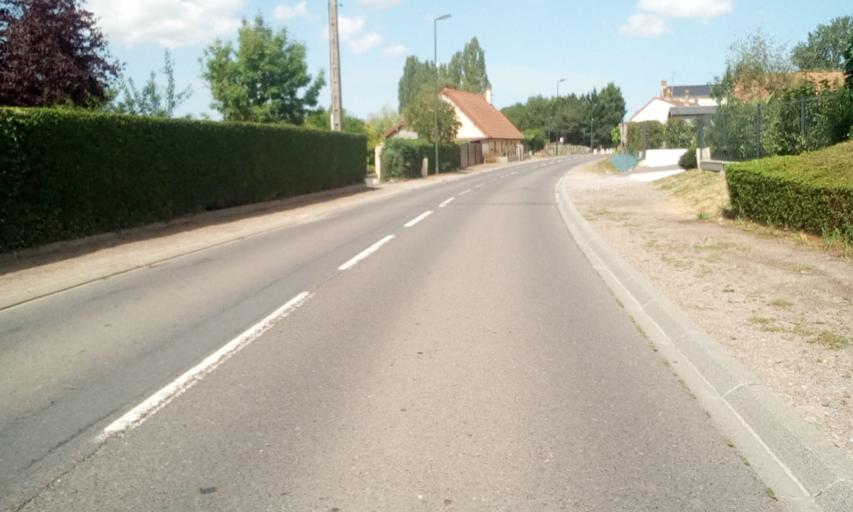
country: FR
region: Lower Normandy
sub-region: Departement du Calvados
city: Argences
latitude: 49.1442
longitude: -0.1639
